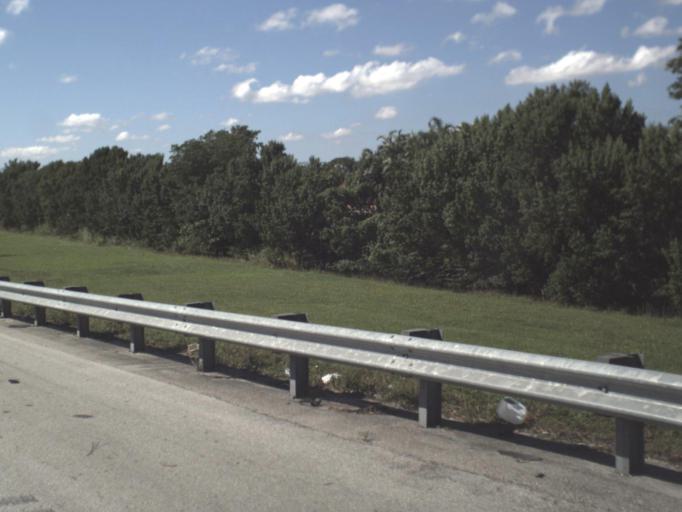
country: US
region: Florida
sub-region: Miami-Dade County
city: Kendale Lakes
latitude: 25.6989
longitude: -80.3844
